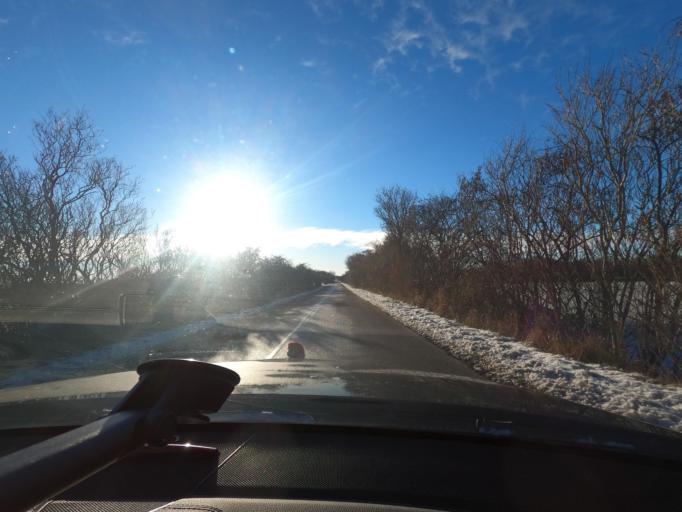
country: DK
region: South Denmark
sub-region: Sonderborg Kommune
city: Horuphav
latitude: 54.8784
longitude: 9.8971
